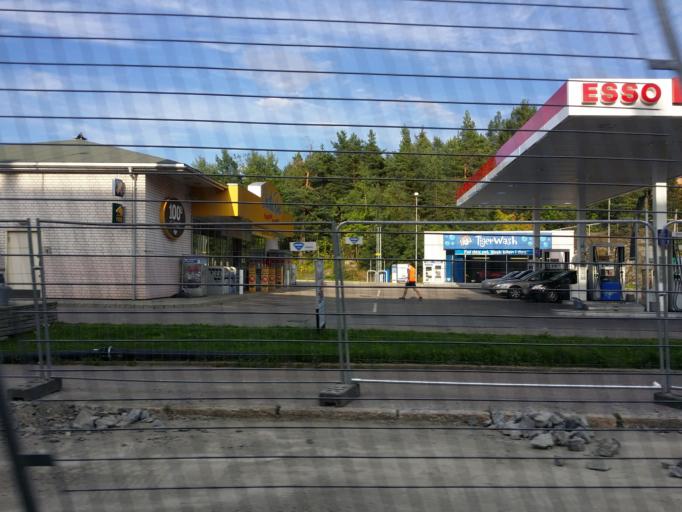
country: NO
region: Akershus
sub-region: Oppegard
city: Kolbotn
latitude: 59.8986
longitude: 10.8521
